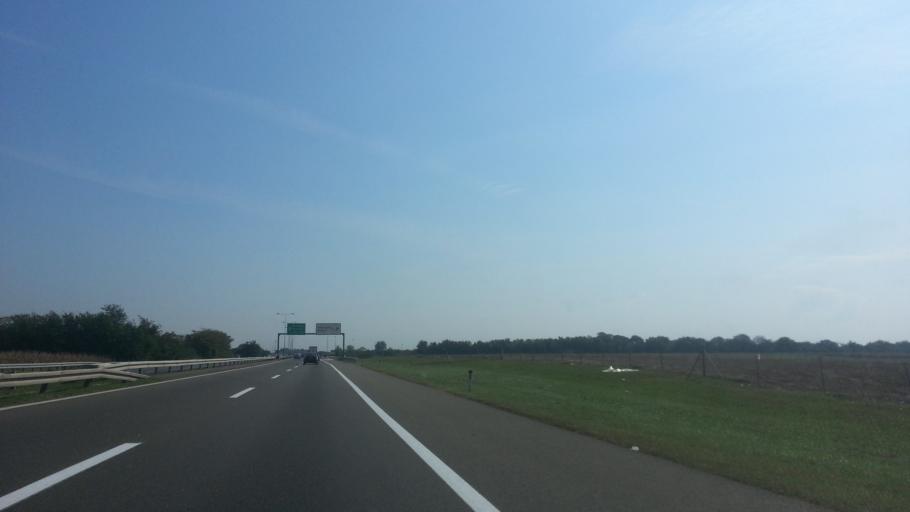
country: RS
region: Central Serbia
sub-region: Belgrade
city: Surcin
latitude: 44.8339
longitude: 20.2703
